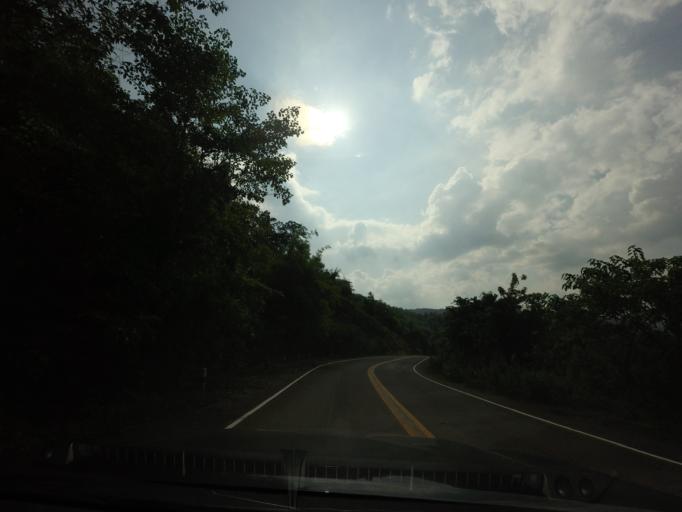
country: TH
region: Nan
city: Na Noi
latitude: 18.2798
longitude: 100.9484
